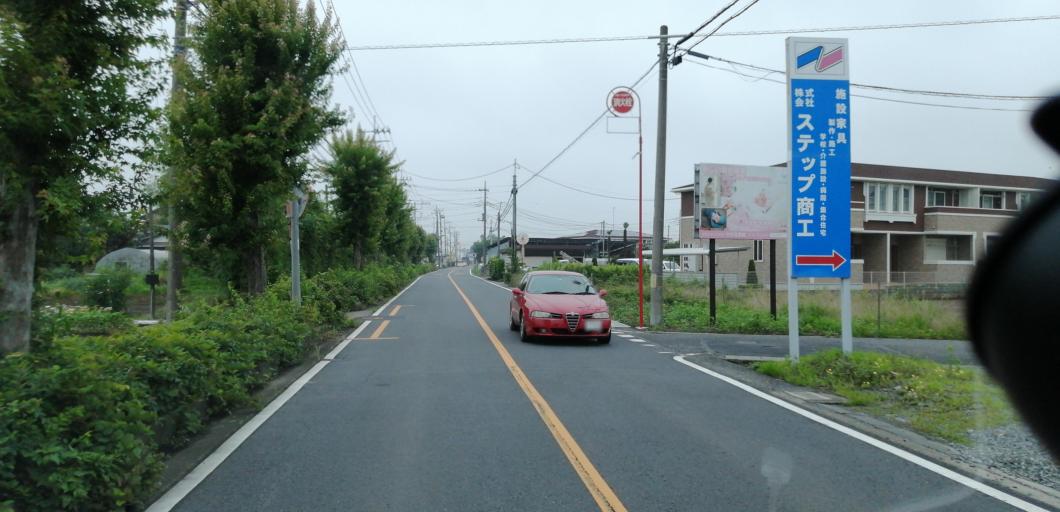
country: JP
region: Saitama
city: Kazo
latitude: 36.1212
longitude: 139.6270
